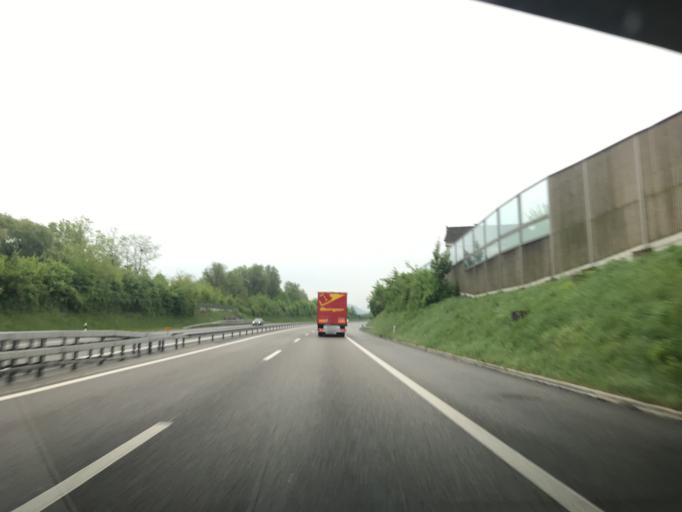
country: CH
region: Aargau
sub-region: Bezirk Zofingen
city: Strengelbach
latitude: 47.2730
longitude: 7.9415
